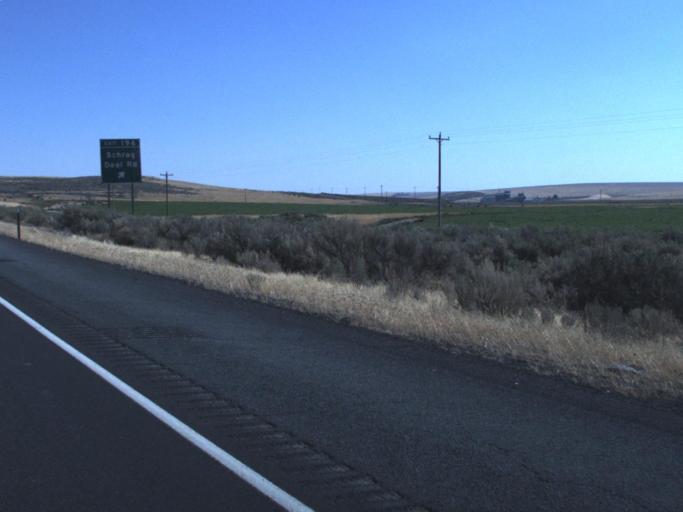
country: US
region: Washington
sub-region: Grant County
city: Warden
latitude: 47.0869
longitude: -118.8825
